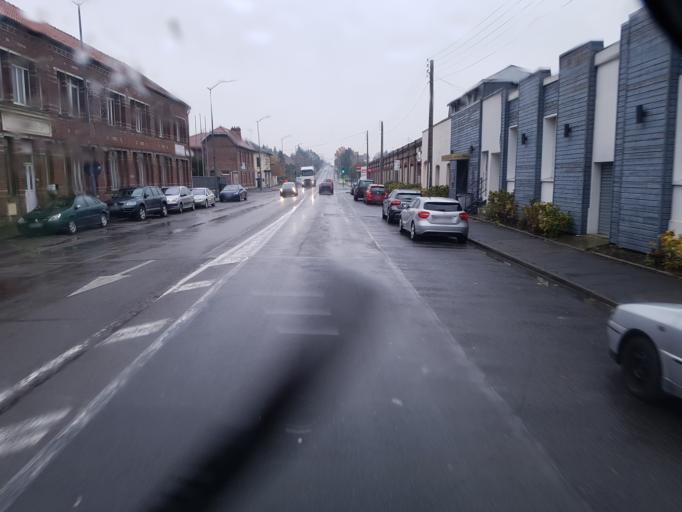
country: FR
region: Picardie
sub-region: Departement de l'Aisne
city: Saint-Quentin
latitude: 49.8581
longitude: 3.2781
